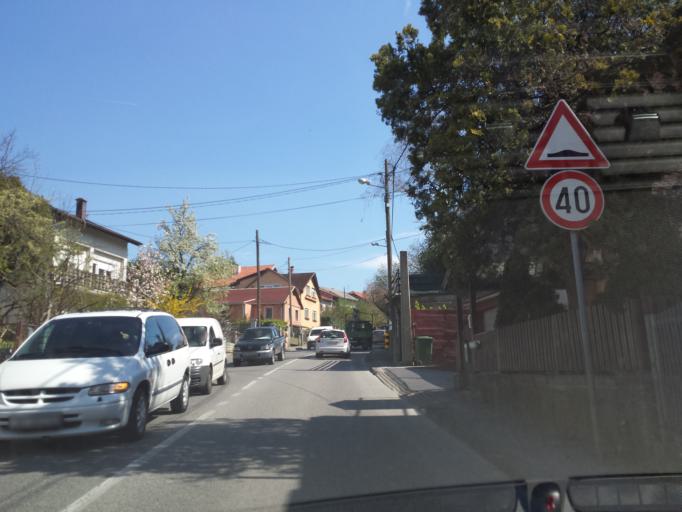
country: HR
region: Grad Zagreb
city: Zagreb
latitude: 45.8587
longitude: 15.9781
